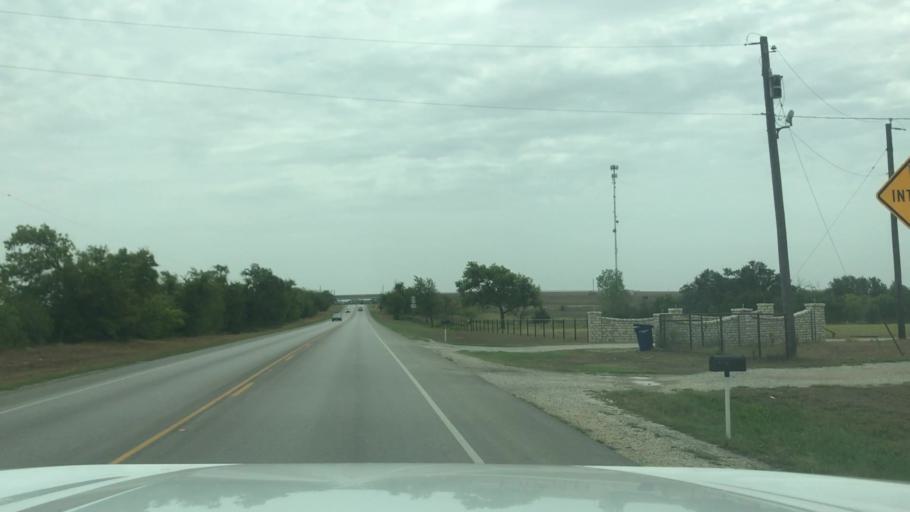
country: US
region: Texas
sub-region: Erath County
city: Dublin
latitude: 32.0953
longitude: -98.3749
